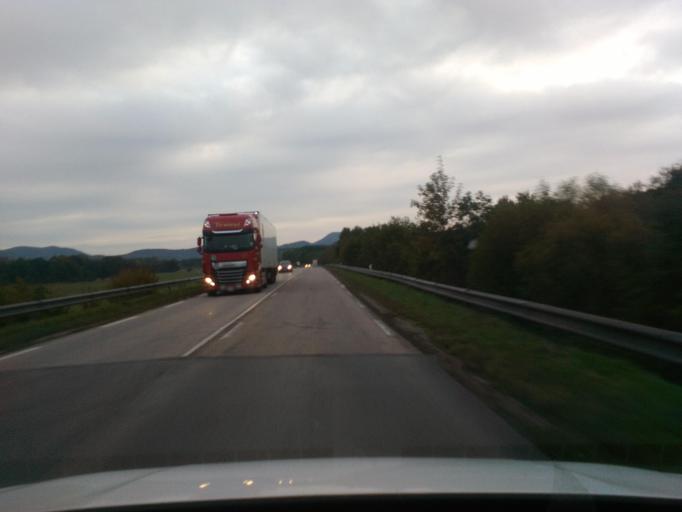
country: FR
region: Lorraine
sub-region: Departement des Vosges
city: Ban-de-Laveline
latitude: 48.2775
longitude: 7.0596
